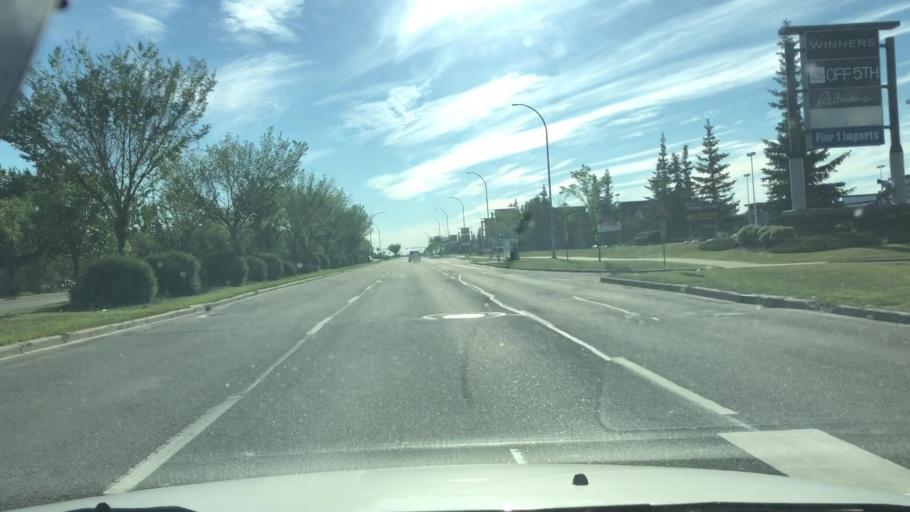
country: CA
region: Alberta
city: St. Albert
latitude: 53.5996
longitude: -113.5534
